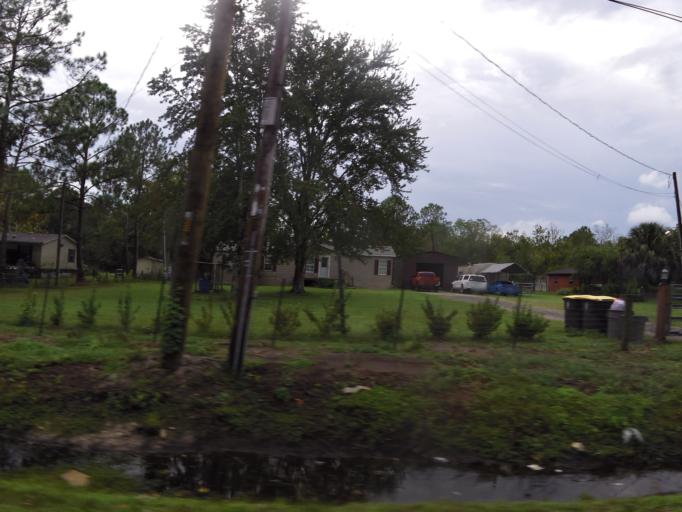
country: US
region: Florida
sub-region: Duval County
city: Baldwin
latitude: 30.3319
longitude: -81.9007
